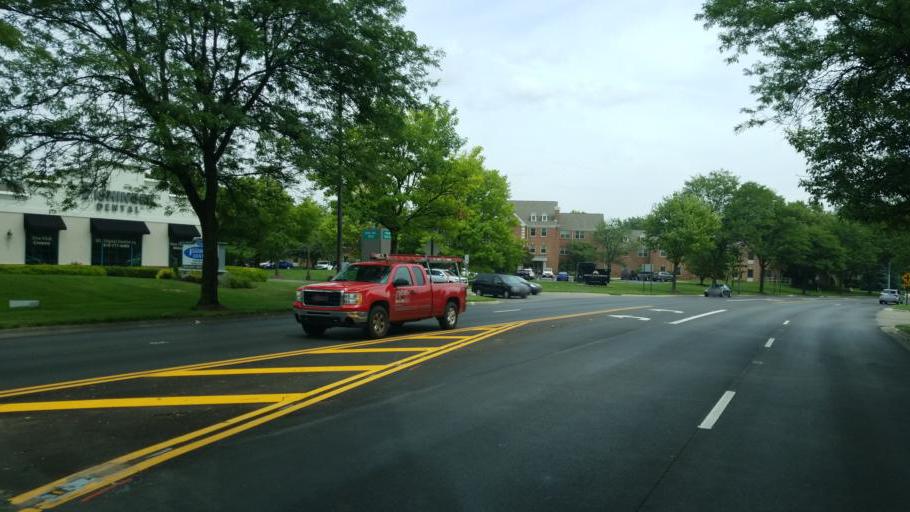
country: US
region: Ohio
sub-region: Franklin County
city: Hilliard
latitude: 40.0269
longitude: -83.1119
